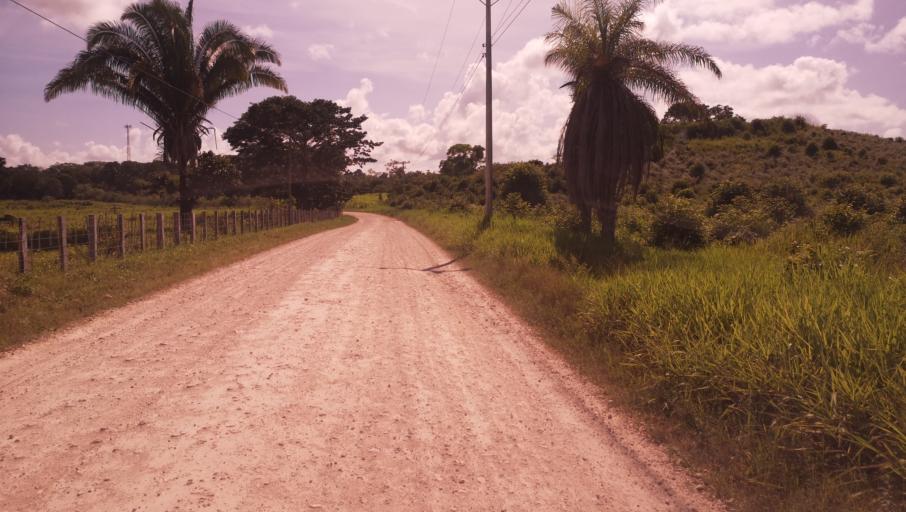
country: GT
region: Peten
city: Dolores
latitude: 16.7902
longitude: -89.3049
